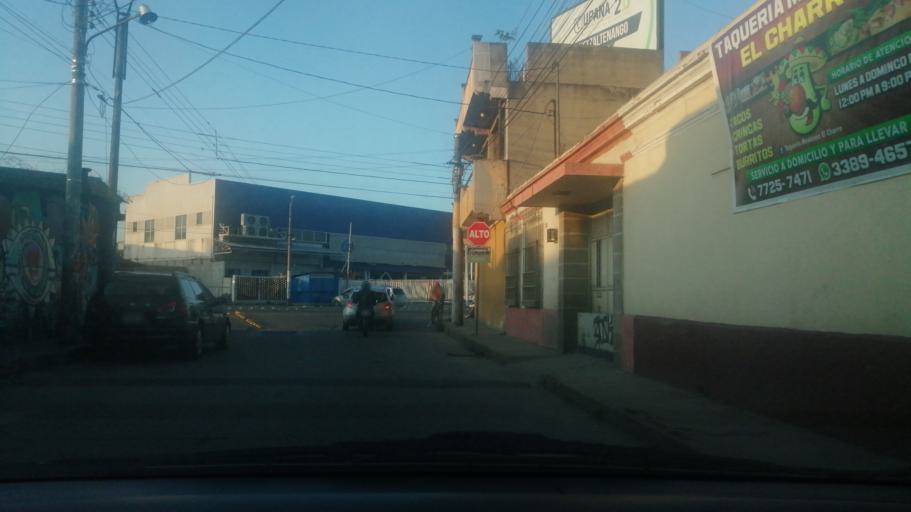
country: GT
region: Quetzaltenango
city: Quetzaltenango
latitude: 14.8343
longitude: -91.5124
